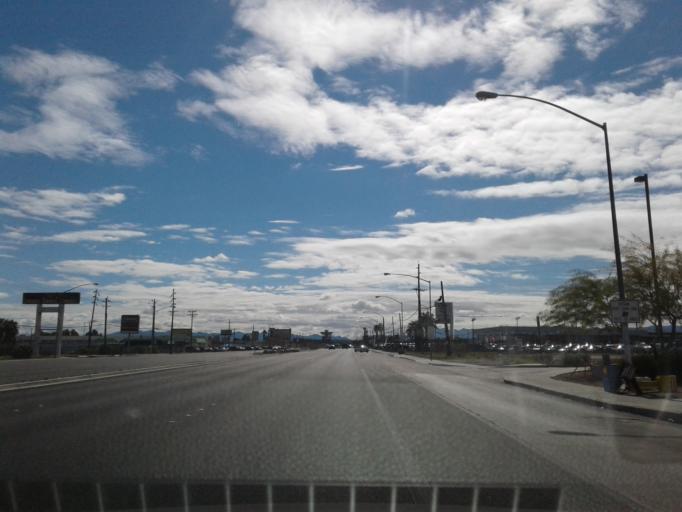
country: US
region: Nevada
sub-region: Clark County
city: Winchester
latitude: 36.1453
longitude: -115.1013
